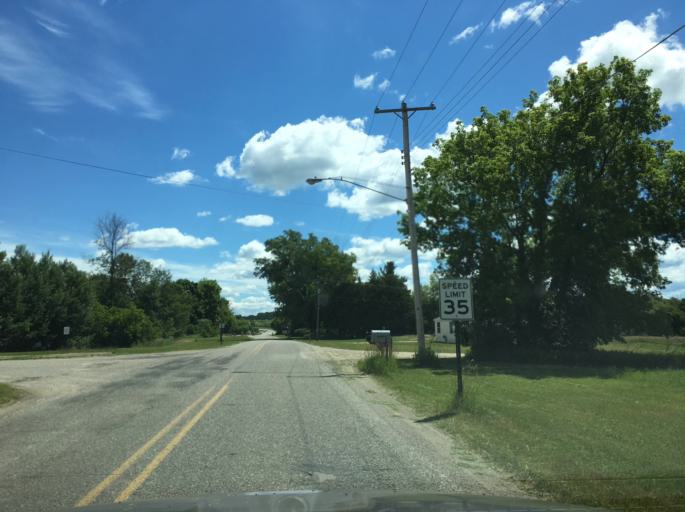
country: US
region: Michigan
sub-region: Osceola County
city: Reed City
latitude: 43.8473
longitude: -85.4376
